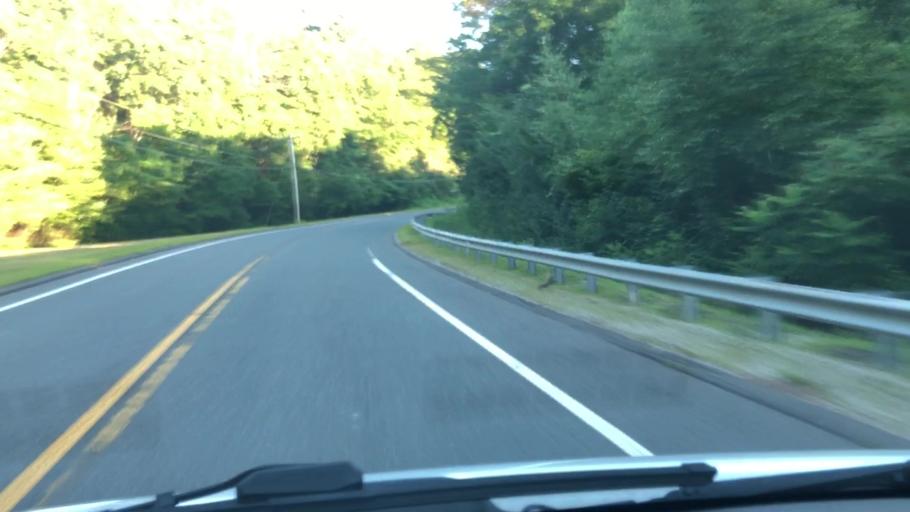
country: US
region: Massachusetts
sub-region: Hampshire County
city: Westhampton
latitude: 42.2823
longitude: -72.7928
